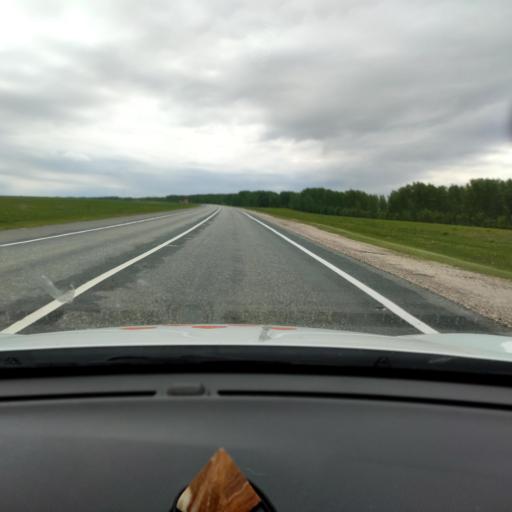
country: RU
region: Tatarstan
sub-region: Alekseyevskiy Rayon
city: Alekseyevskoye
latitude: 55.3942
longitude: 49.8739
